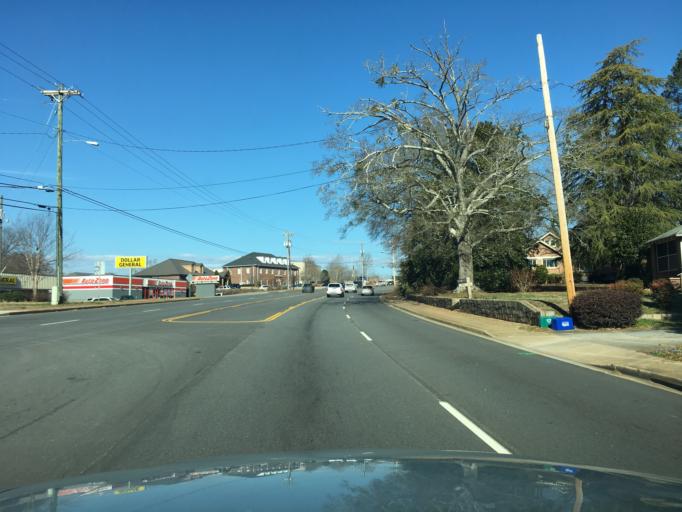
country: US
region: South Carolina
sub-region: Pickens County
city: Pickens
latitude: 34.8782
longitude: -82.7011
